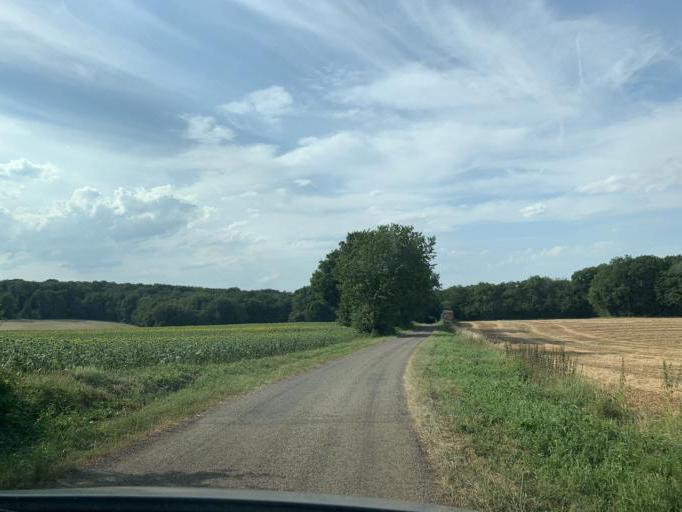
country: FR
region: Bourgogne
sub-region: Departement de l'Yonne
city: Fontenailles
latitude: 47.5040
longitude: 3.4289
